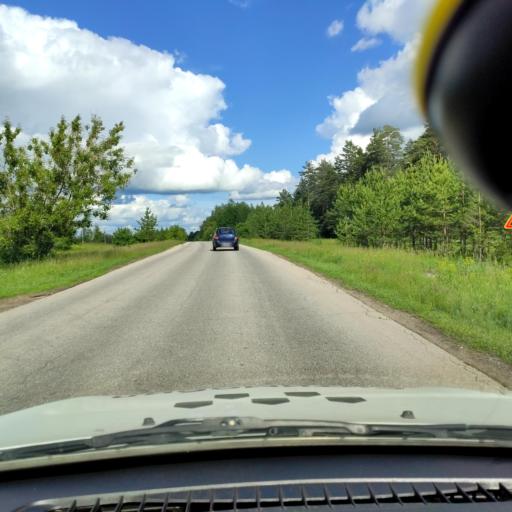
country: RU
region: Samara
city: Povolzhskiy
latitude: 53.6474
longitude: 49.7382
